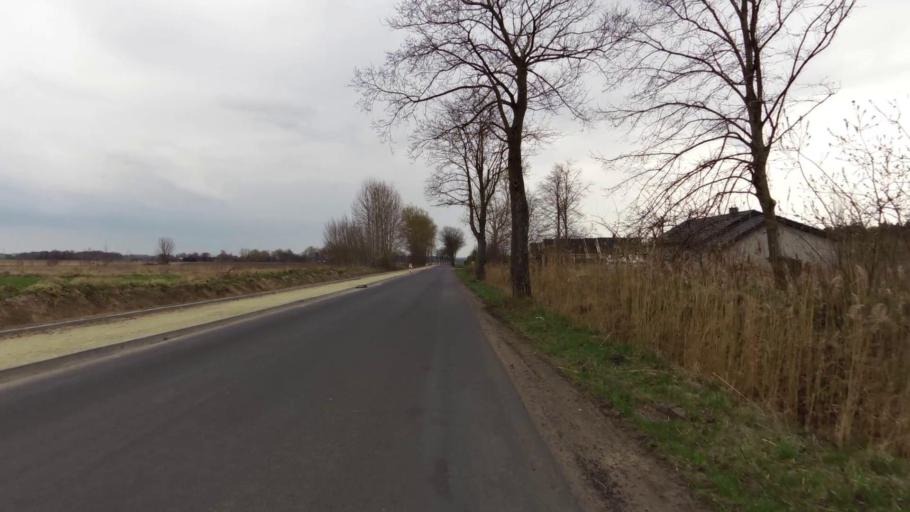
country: PL
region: West Pomeranian Voivodeship
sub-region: Powiat koszalinski
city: Sianow
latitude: 54.2799
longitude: 16.2201
